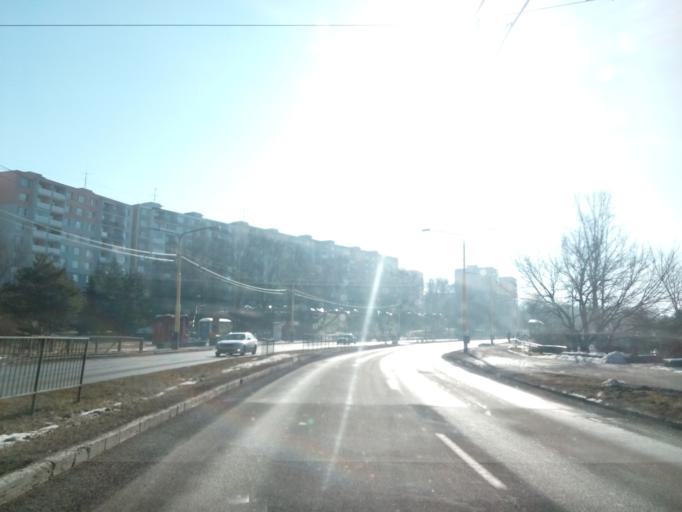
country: SK
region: Kosicky
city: Kosice
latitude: 48.7429
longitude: 21.2797
